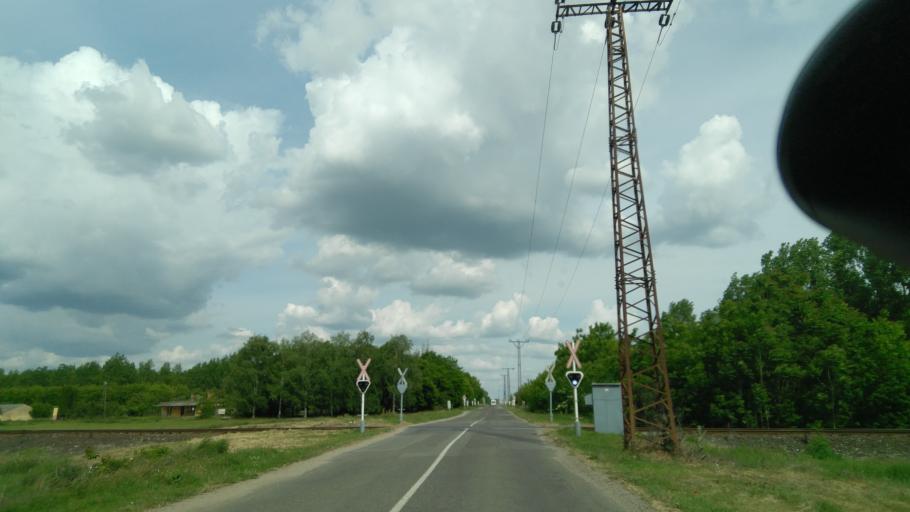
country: HU
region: Bekes
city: Mezohegyes
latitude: 46.3157
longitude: 20.8303
